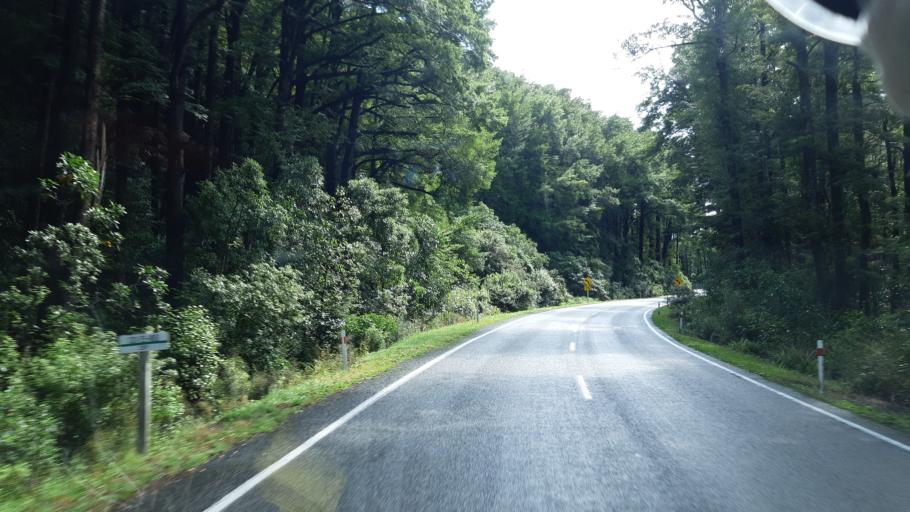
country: NZ
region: West Coast
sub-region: Buller District
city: Westport
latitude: -42.3550
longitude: 172.2411
